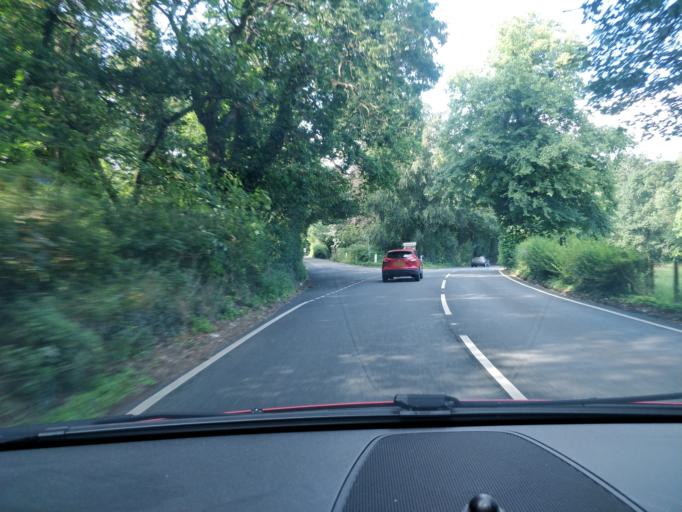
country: GB
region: Wales
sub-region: Conwy
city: Llansantffraid Glan Conwy
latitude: 53.2421
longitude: -3.7967
